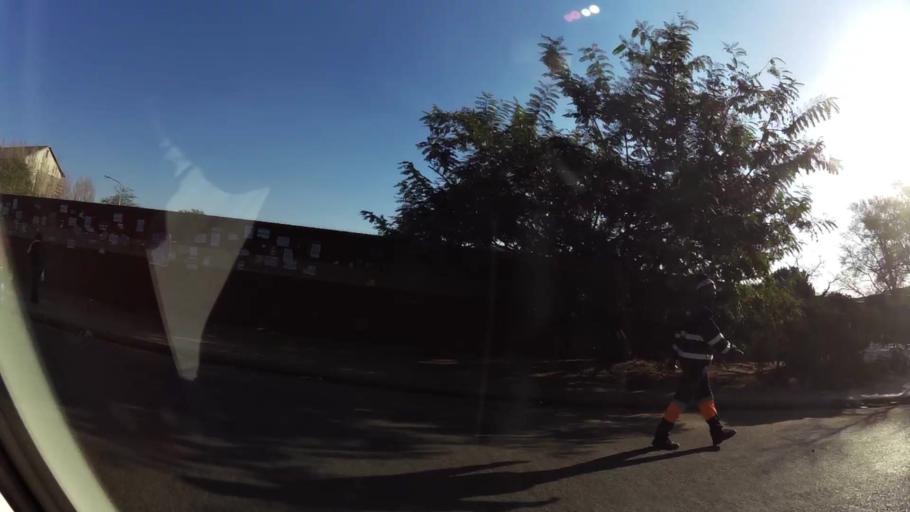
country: ZA
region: North-West
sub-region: Bojanala Platinum District Municipality
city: Rustenburg
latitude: -25.6703
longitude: 27.2381
